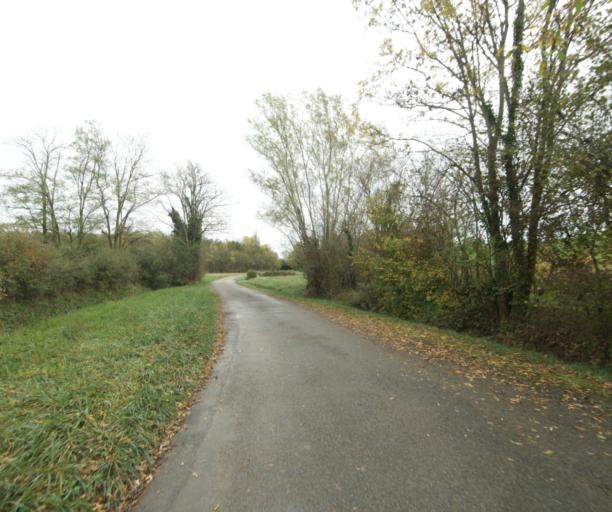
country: FR
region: Rhone-Alpes
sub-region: Departement de l'Ain
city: Pont-de-Vaux
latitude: 46.4732
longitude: 4.8784
